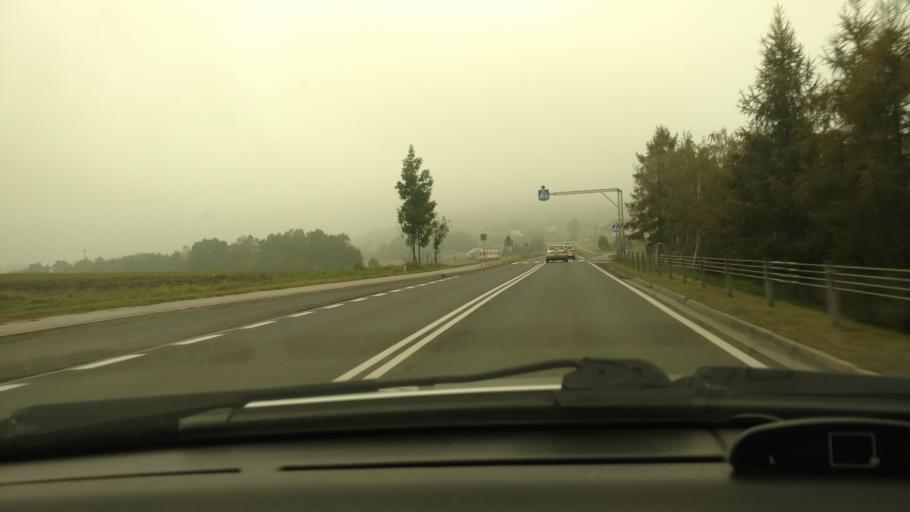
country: PL
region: Lesser Poland Voivodeship
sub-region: Powiat nowosadecki
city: Kamionka Wielka
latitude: 49.6132
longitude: 20.8728
